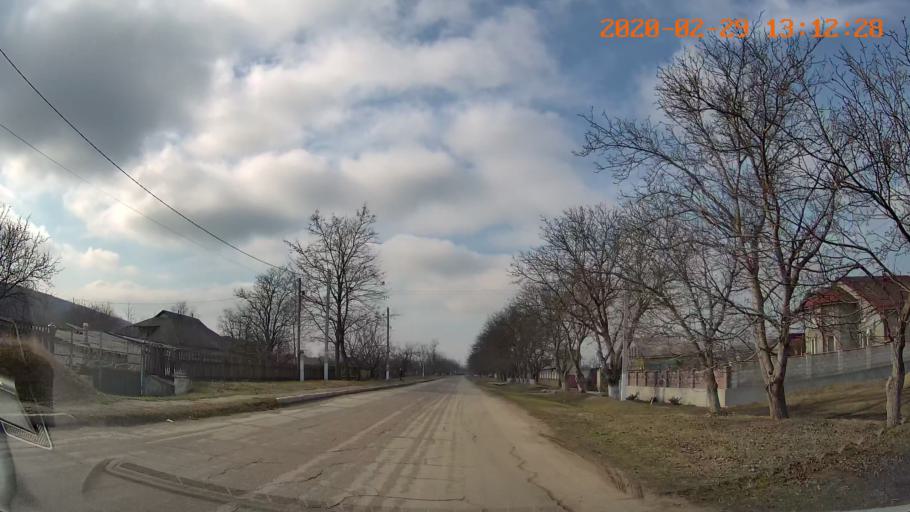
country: MD
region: Telenesti
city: Camenca
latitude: 48.0130
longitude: 28.6952
